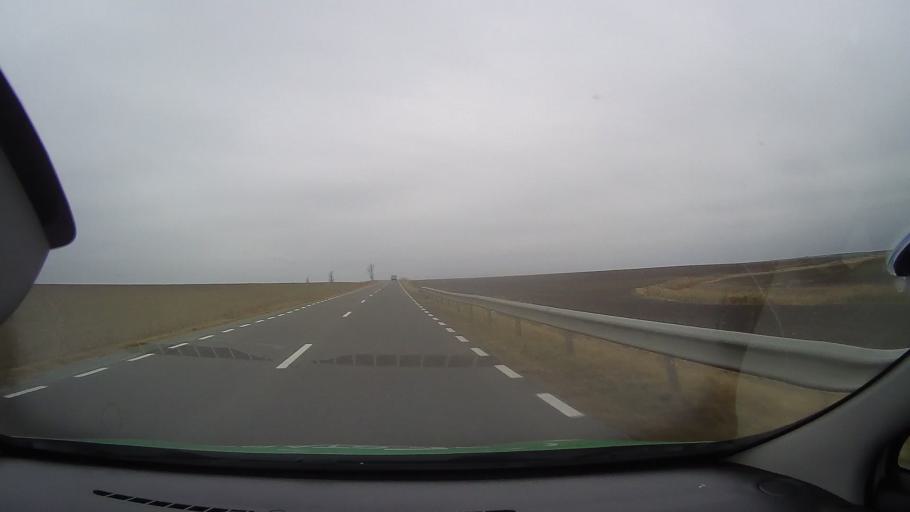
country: RO
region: Ialomita
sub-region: Comuna Scanteia
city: Iazu
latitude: 44.7191
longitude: 27.4211
